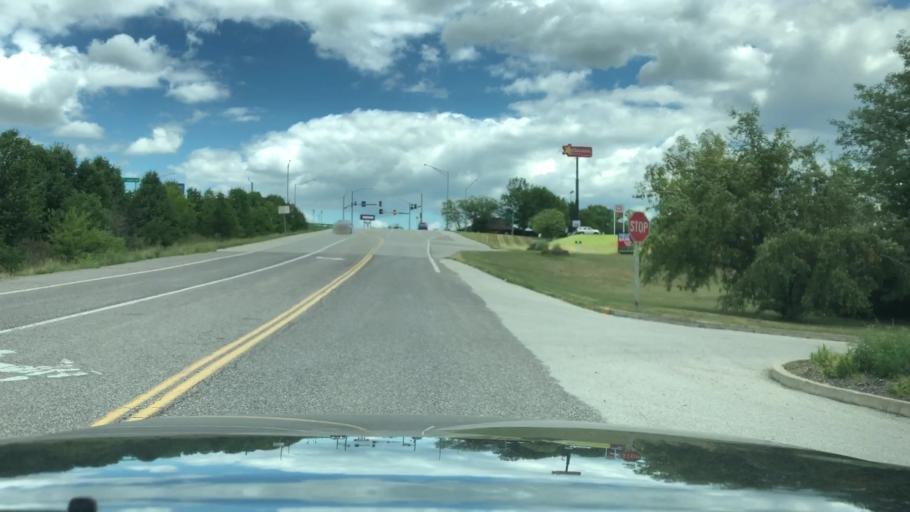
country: US
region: Missouri
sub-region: Saint Charles County
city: Lake Saint Louis
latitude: 38.8035
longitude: -90.7730
